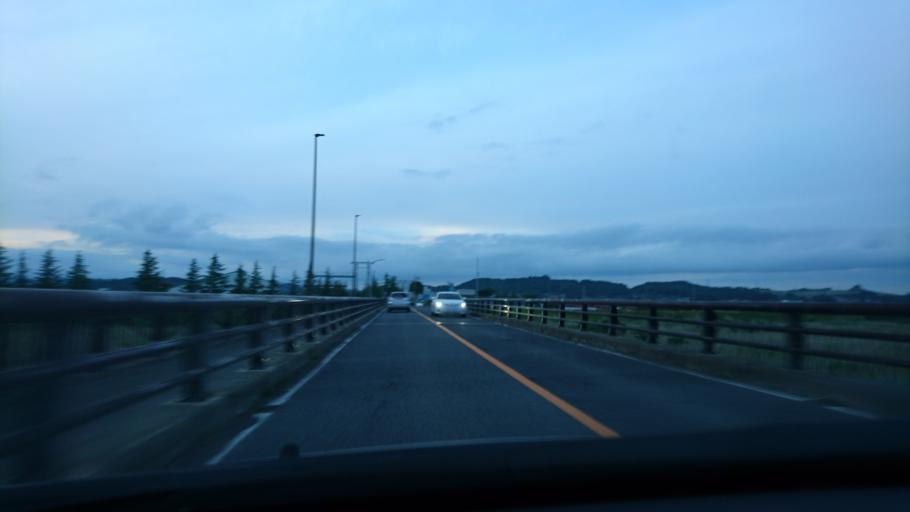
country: JP
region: Iwate
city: Ichinoseki
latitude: 38.7977
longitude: 140.9788
